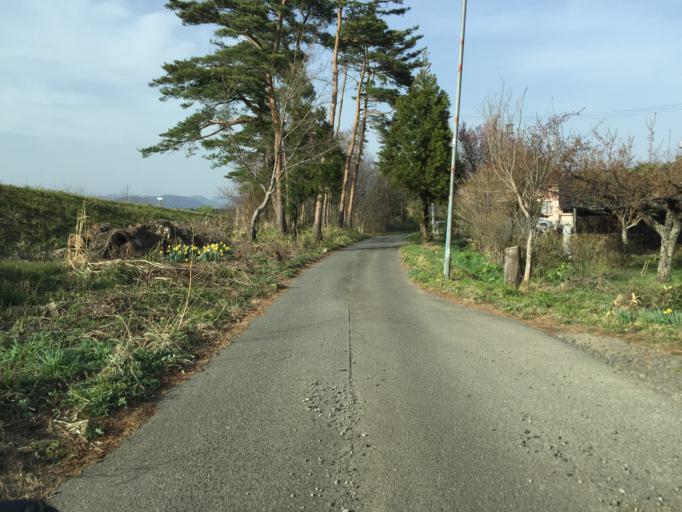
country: JP
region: Fukushima
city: Fukushima-shi
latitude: 37.7246
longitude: 140.3716
